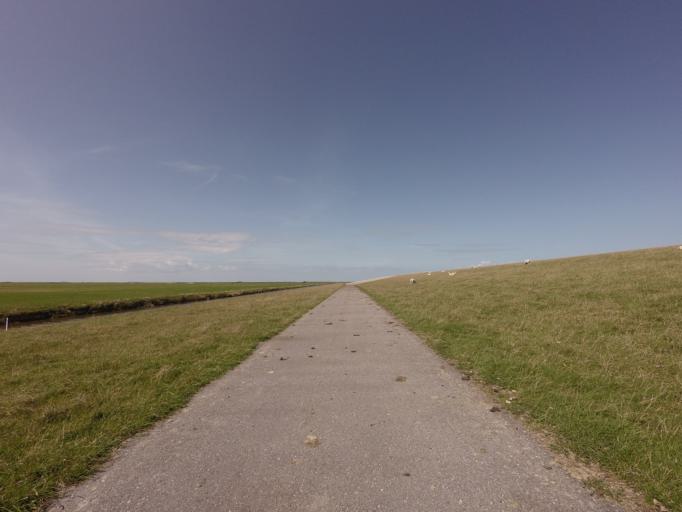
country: NL
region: Friesland
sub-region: Gemeente Dongeradeel
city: Holwerd
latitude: 53.3676
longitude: 5.8604
